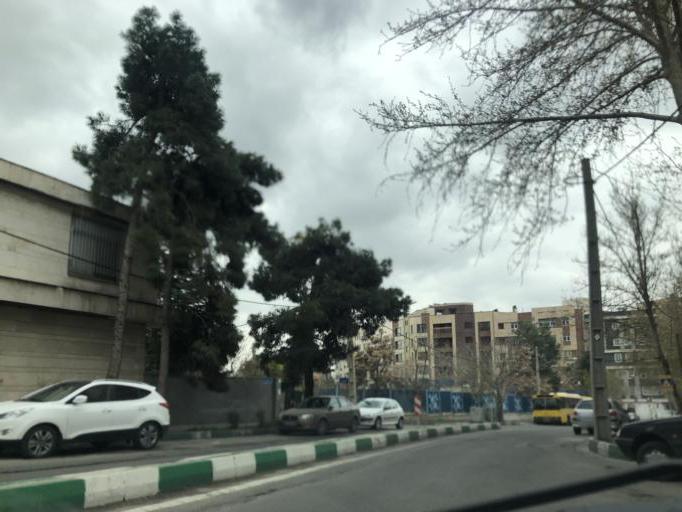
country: IR
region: Tehran
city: Tajrish
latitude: 35.7794
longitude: 51.4651
